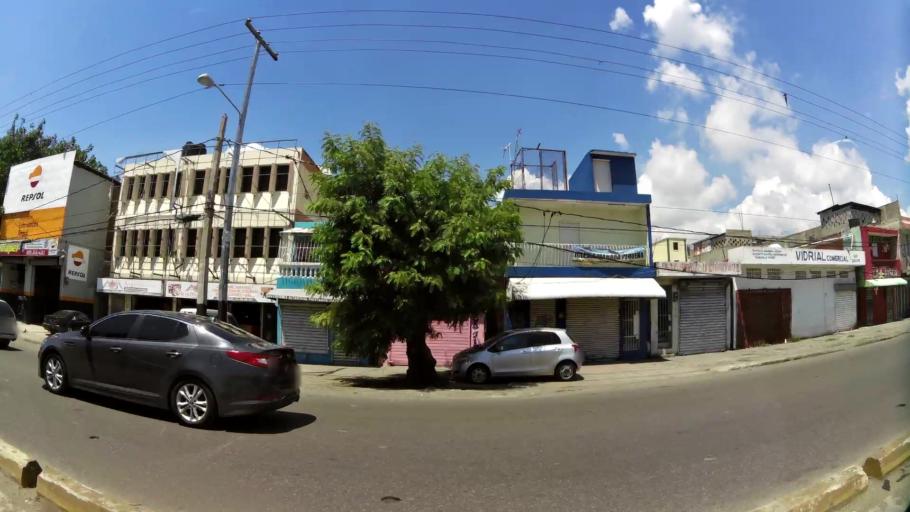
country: DO
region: Nacional
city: Ensanche Luperon
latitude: 18.5018
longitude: -69.8870
